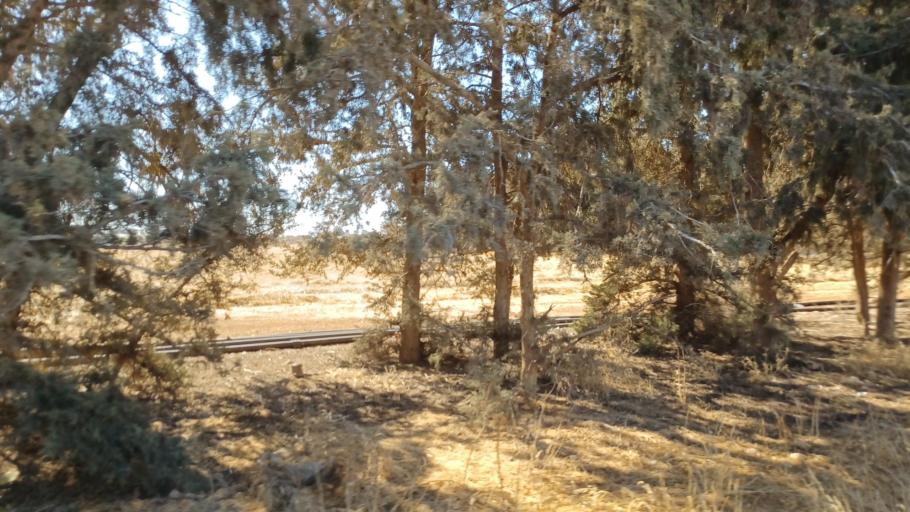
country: CY
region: Larnaka
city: Pergamos
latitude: 35.0514
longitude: 33.7048
